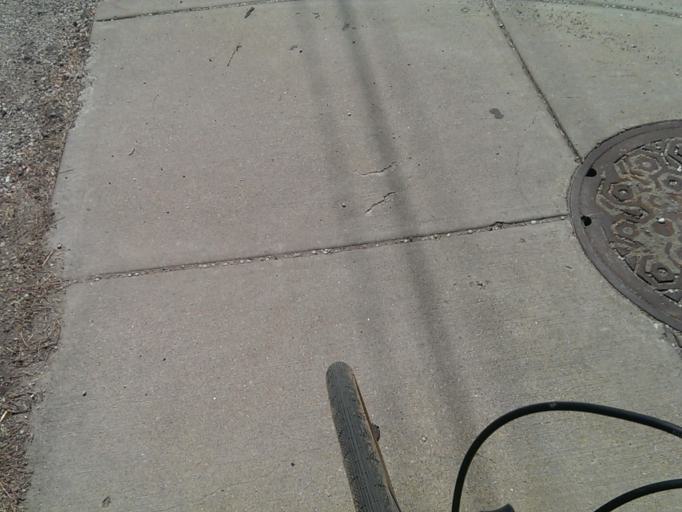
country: US
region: Kansas
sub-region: Johnson County
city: Leawood
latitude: 38.9888
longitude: -94.5943
